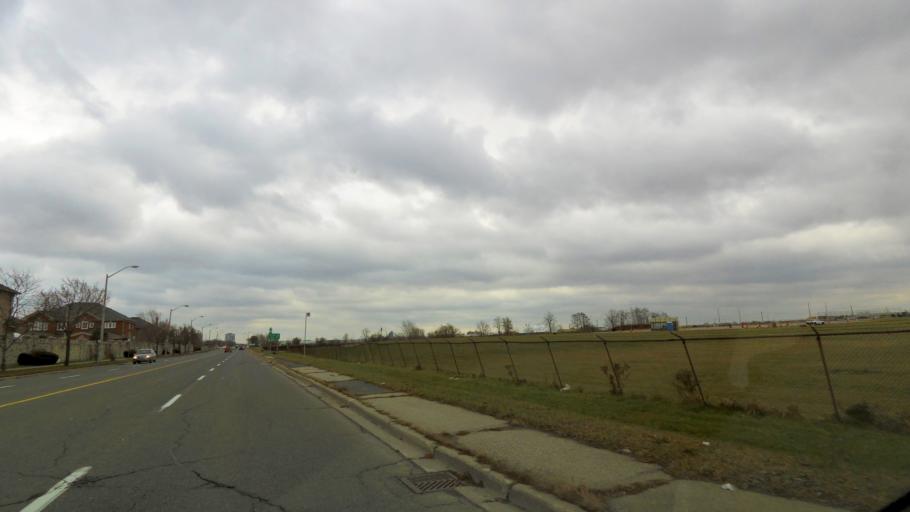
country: CA
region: Ontario
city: North York
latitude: 43.7463
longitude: -79.4539
